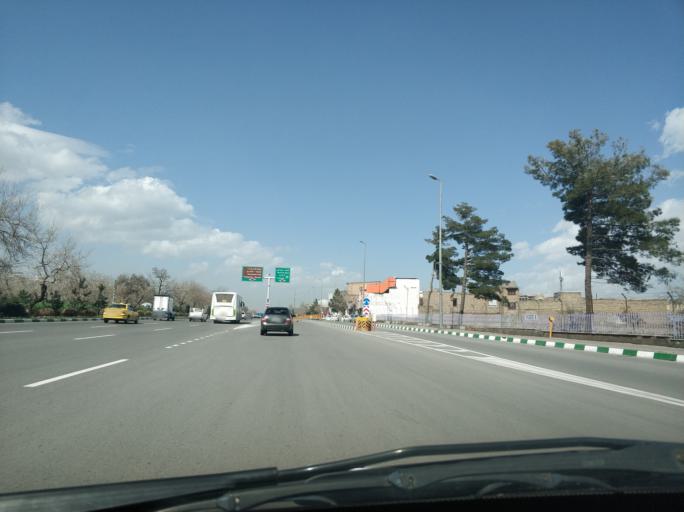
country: IR
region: Razavi Khorasan
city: Torqabeh
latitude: 36.3417
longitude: 59.4567
